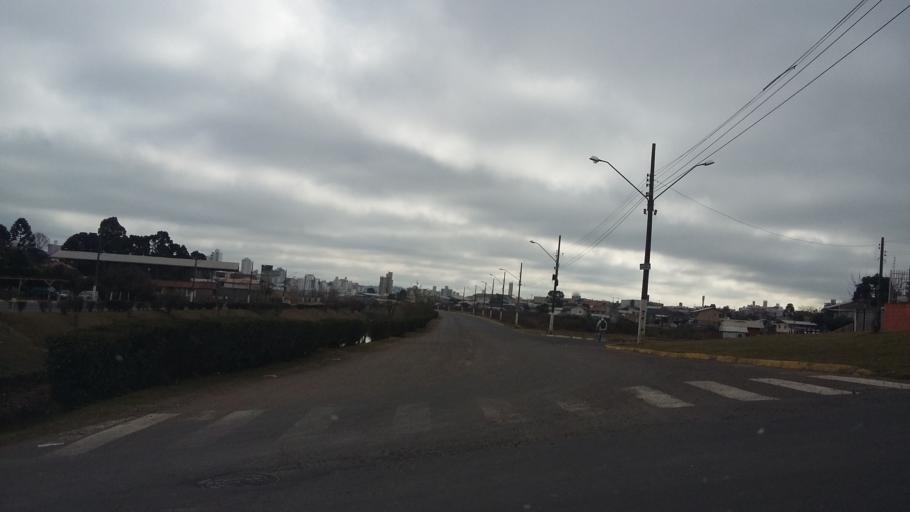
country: BR
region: Santa Catarina
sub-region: Lages
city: Lages
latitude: -27.8338
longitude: -50.3206
